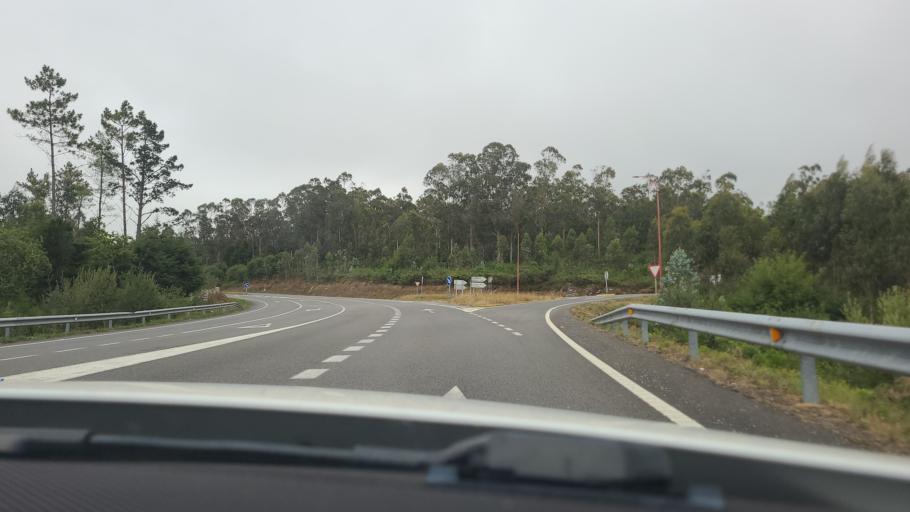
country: ES
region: Galicia
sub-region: Provincia da Coruna
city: Dumbria
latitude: 43.0166
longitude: -9.1216
